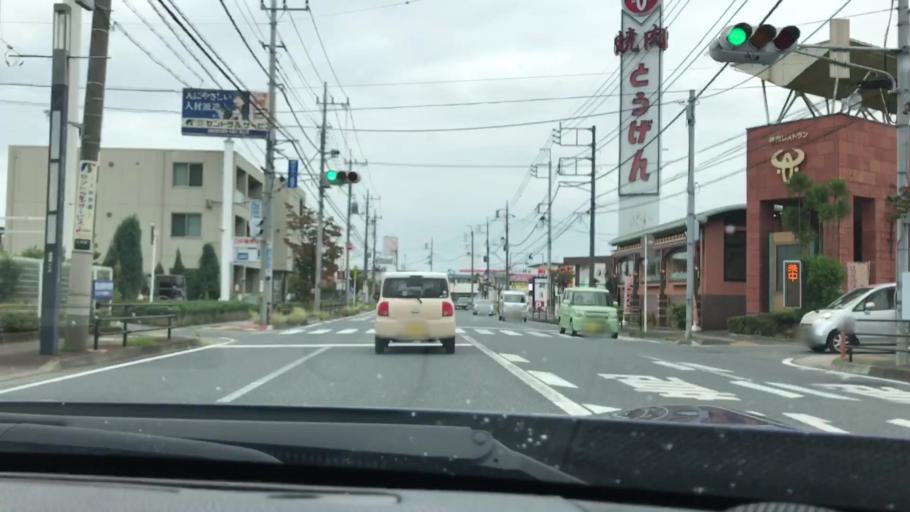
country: JP
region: Gunma
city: Maebashi-shi
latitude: 36.3738
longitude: 139.0453
